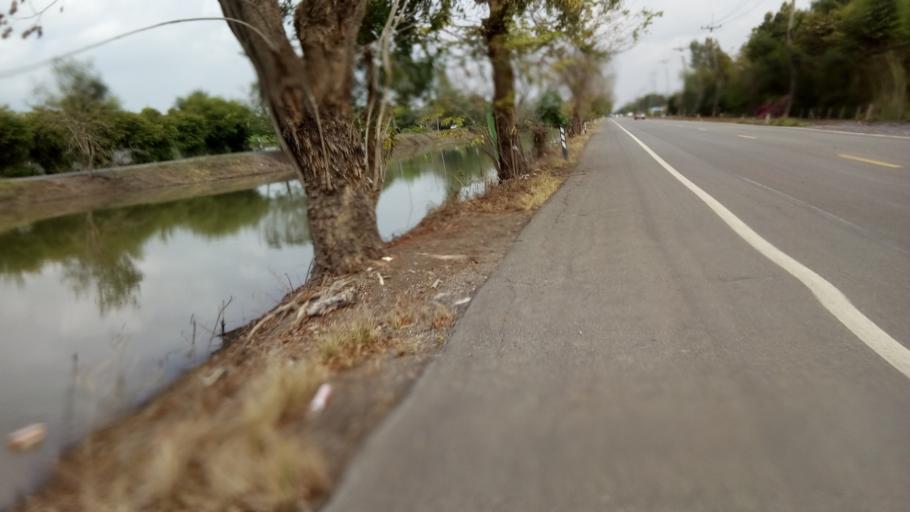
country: TH
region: Pathum Thani
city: Nong Suea
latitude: 14.1763
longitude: 100.8236
